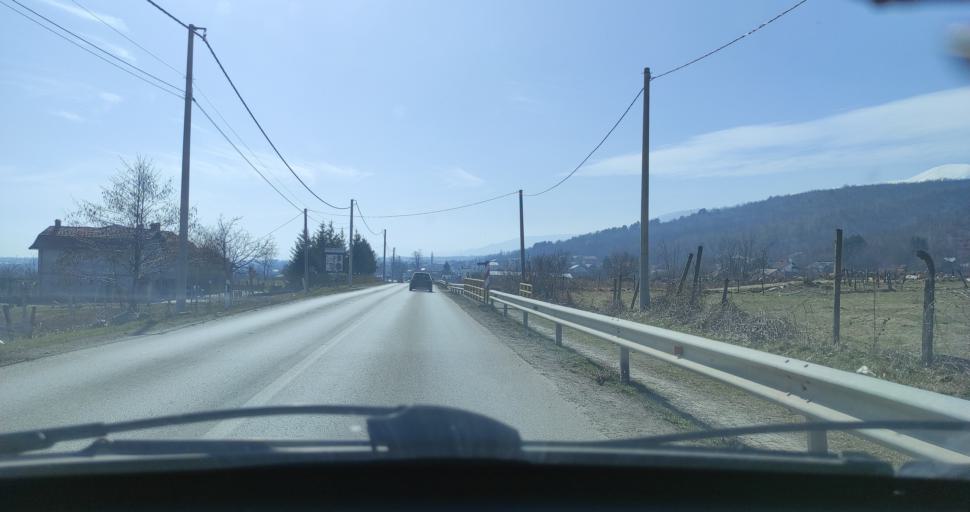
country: XK
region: Gjakova
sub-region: Komuna e Decanit
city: Strellc i Eperm
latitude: 42.5732
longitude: 20.2939
